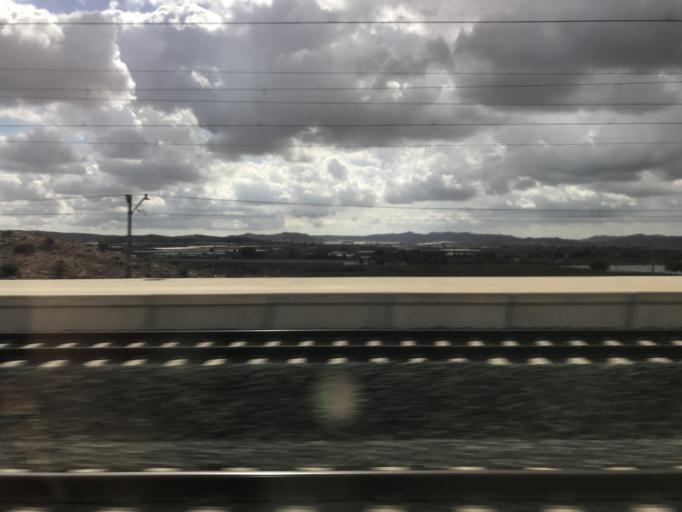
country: ES
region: Valencia
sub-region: Provincia de Alicante
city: Monforte del Cid
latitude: 38.4056
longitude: -0.7058
